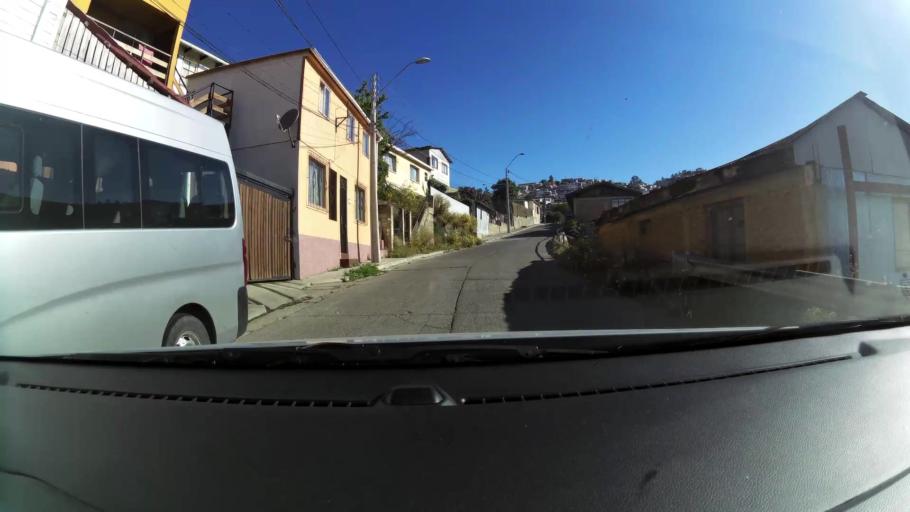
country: CL
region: Valparaiso
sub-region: Provincia de Valparaiso
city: Valparaiso
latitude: -33.0566
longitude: -71.6185
